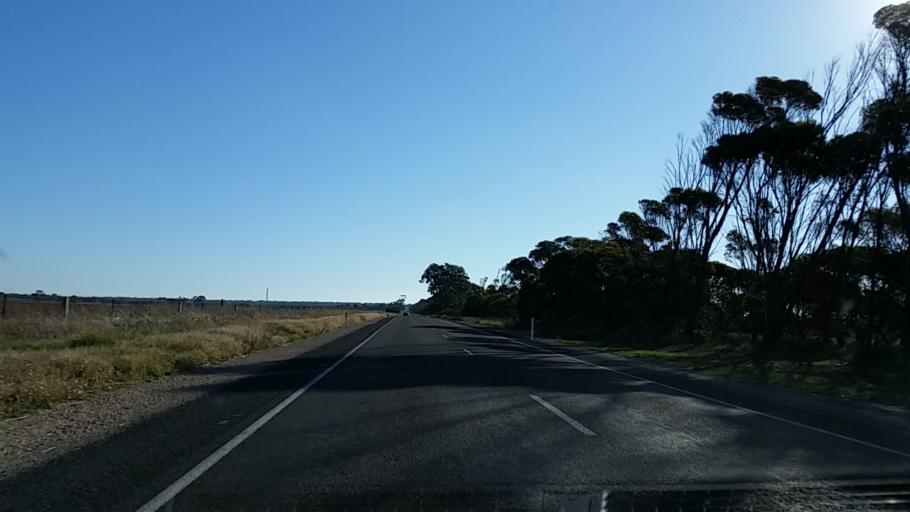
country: AU
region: South Australia
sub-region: Mount Barker
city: Callington
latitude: -35.1166
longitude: 139.1168
